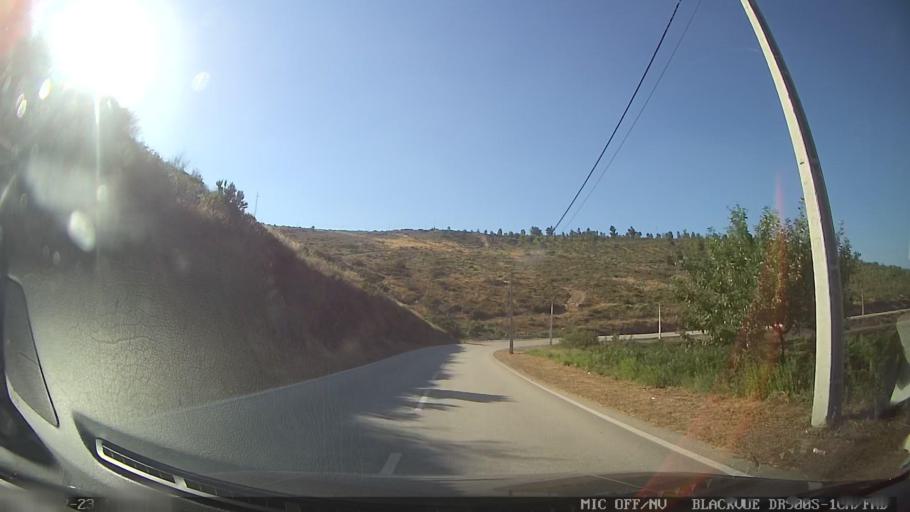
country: PT
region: Viseu
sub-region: Sao Joao da Pesqueira
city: Sao Joao da Pesqueira
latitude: 41.1596
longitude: -7.4364
